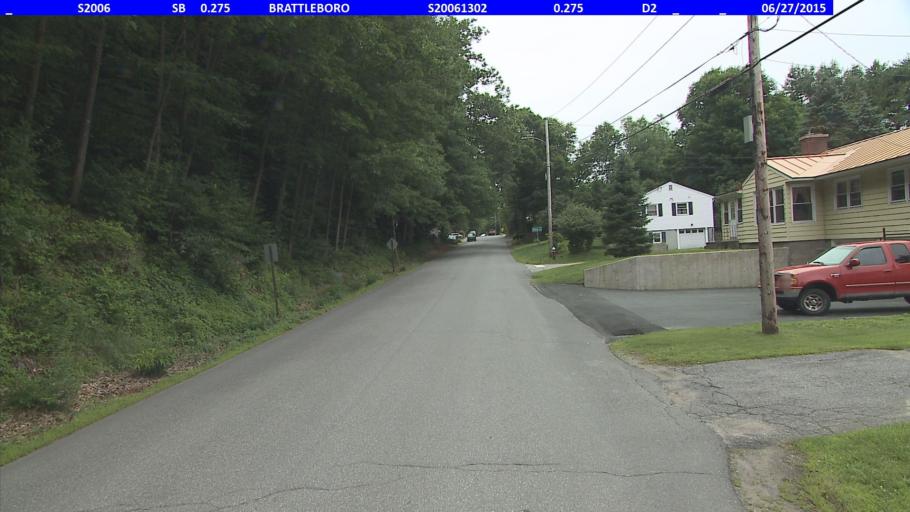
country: US
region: Vermont
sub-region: Windham County
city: Brattleboro
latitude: 42.8562
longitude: -72.5687
